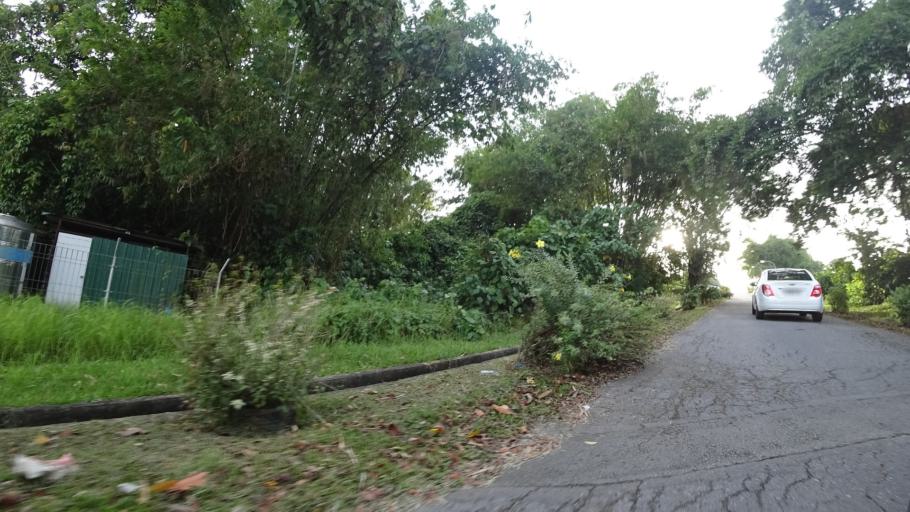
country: BN
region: Brunei and Muara
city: Bandar Seri Begawan
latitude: 4.8891
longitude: 114.8375
